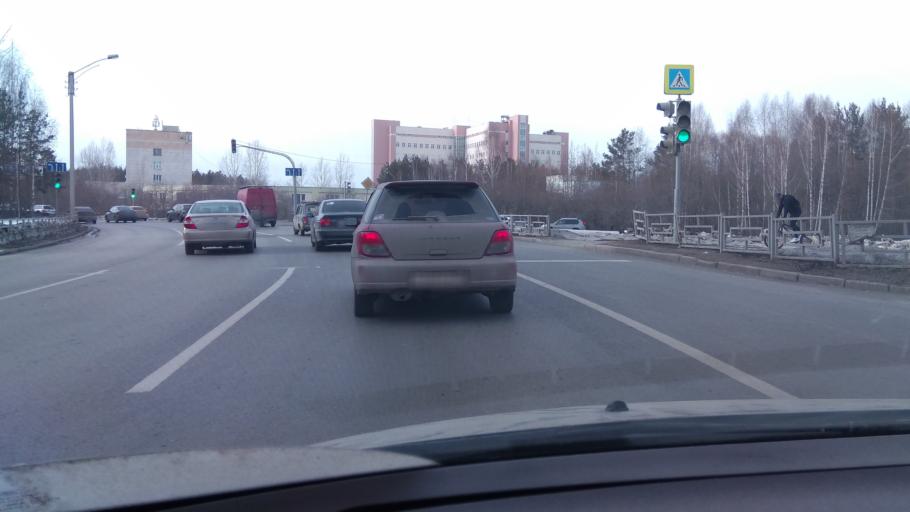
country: RU
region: Sverdlovsk
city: Sovkhoznyy
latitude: 56.8051
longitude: 60.5411
